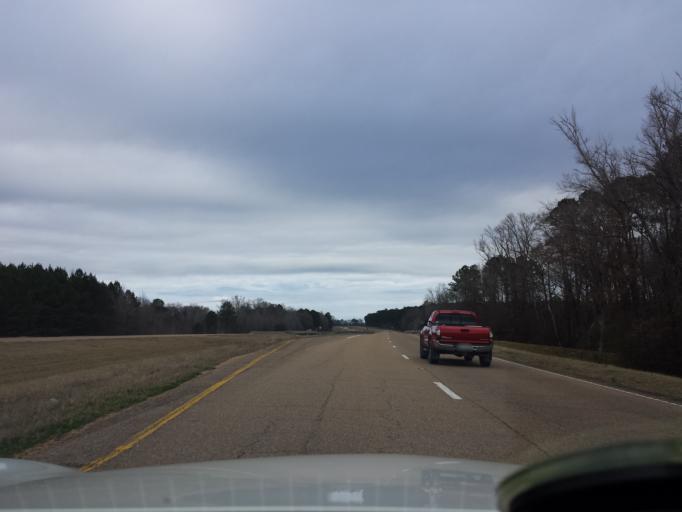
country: US
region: Mississippi
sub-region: Oktibbeha County
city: Starkville
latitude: 33.2972
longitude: -88.9070
